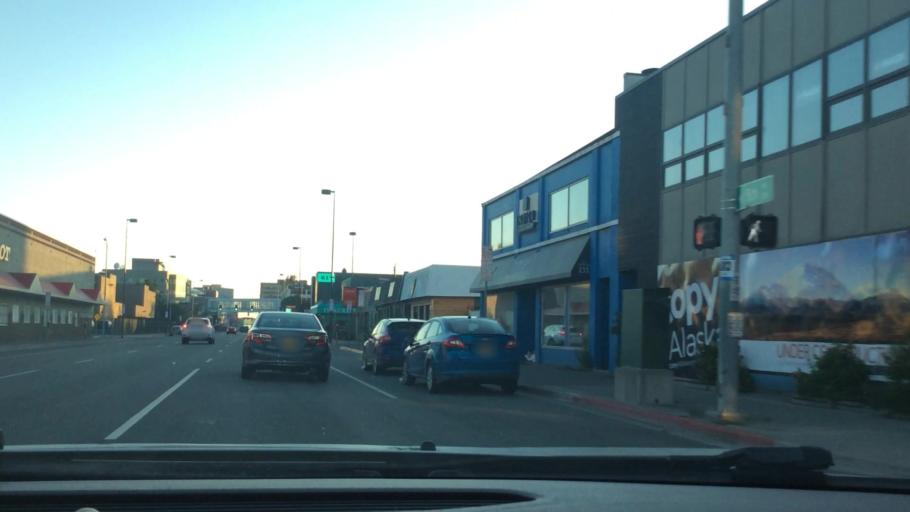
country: US
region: Alaska
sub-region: Anchorage Municipality
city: Anchorage
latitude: 61.2176
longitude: -149.8792
